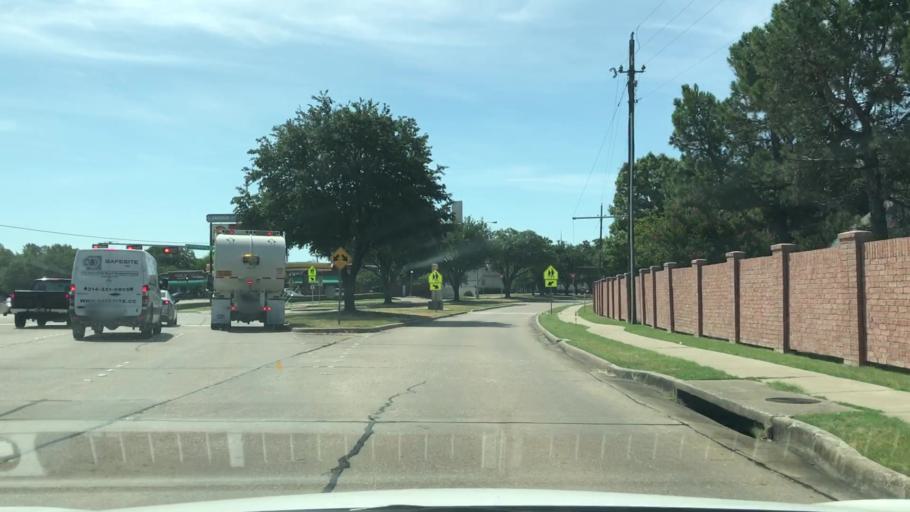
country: US
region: Texas
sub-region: Dallas County
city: Garland
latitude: 32.9408
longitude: -96.6408
